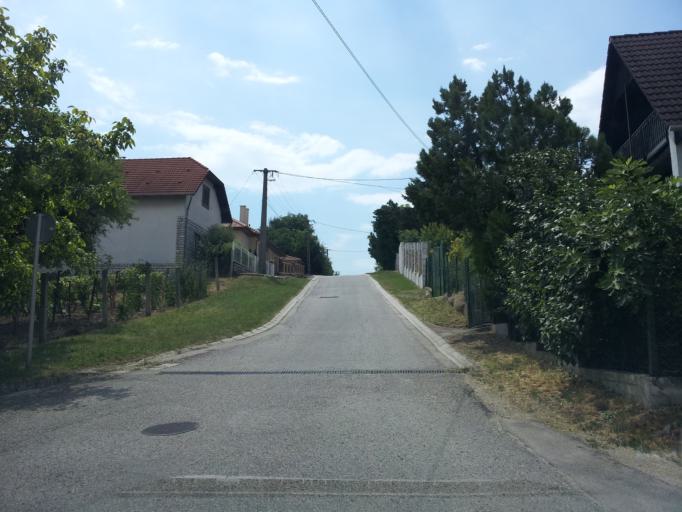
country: HU
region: Veszprem
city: Balatonalmadi
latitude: 47.0391
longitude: 18.0157
